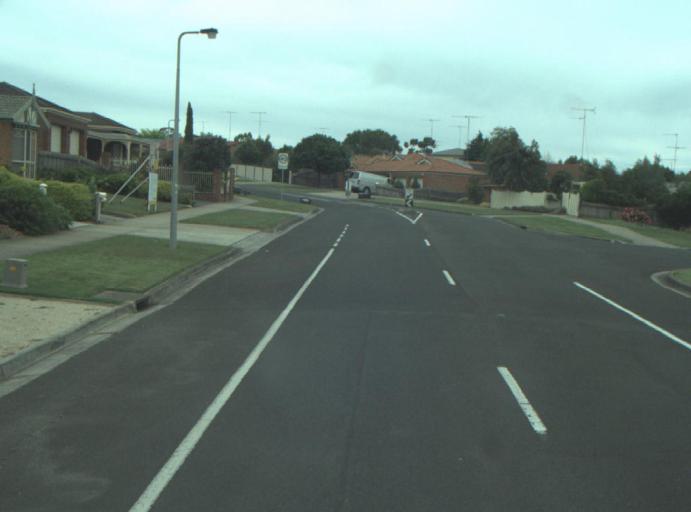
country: AU
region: Victoria
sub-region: Greater Geelong
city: Leopold
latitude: -38.1841
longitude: 144.4612
